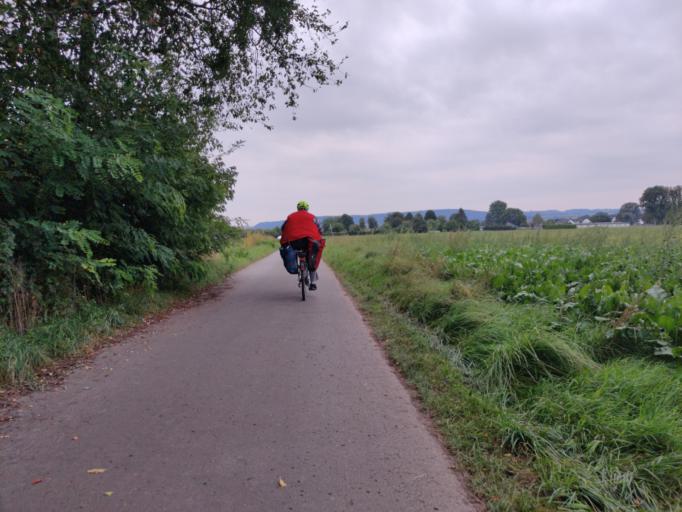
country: DE
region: Lower Saxony
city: Holzminden
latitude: 51.8404
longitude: 9.4426
